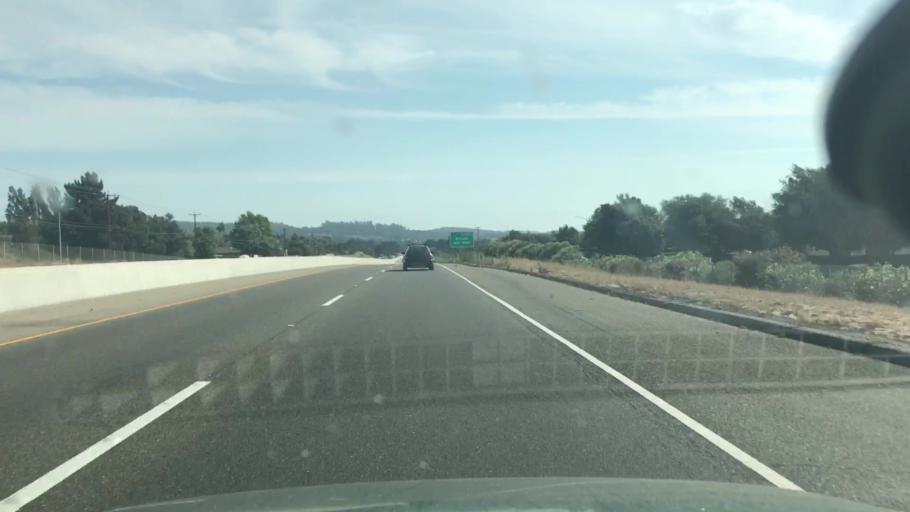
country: US
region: California
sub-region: Santa Barbara County
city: Orcutt
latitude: 34.8740
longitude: -120.4367
